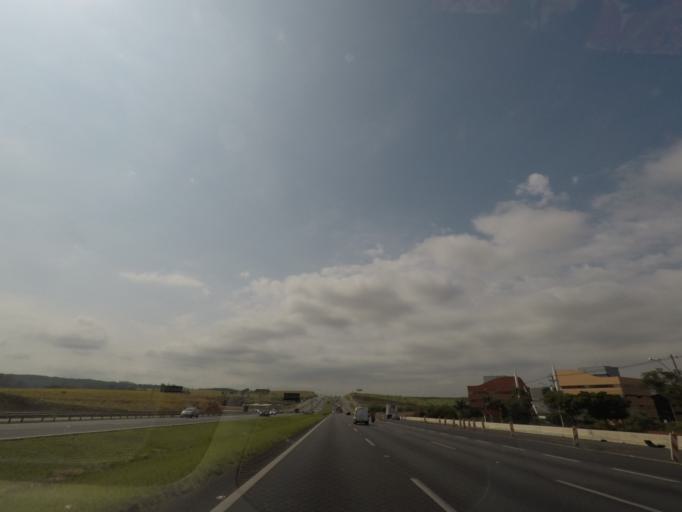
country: BR
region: Sao Paulo
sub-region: Campinas
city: Campinas
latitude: -22.8643
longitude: -47.0212
